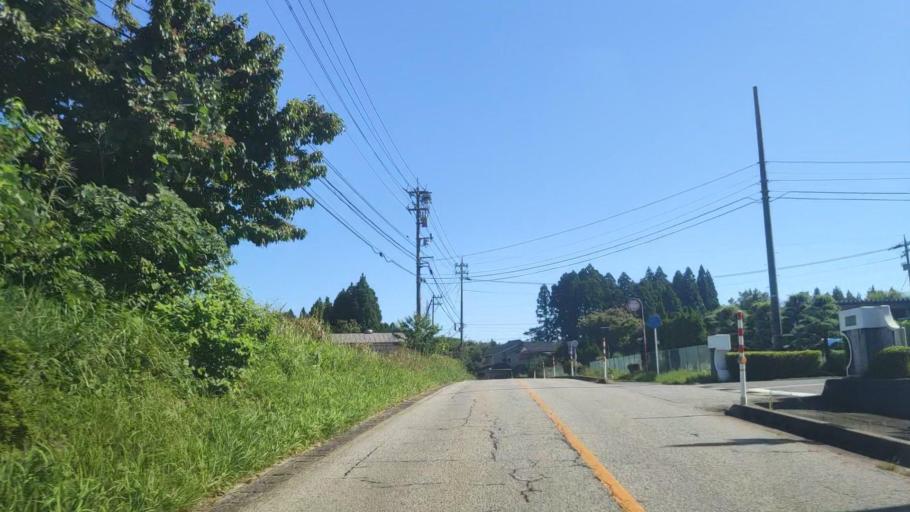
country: JP
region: Ishikawa
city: Nanao
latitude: 37.3444
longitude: 137.2280
